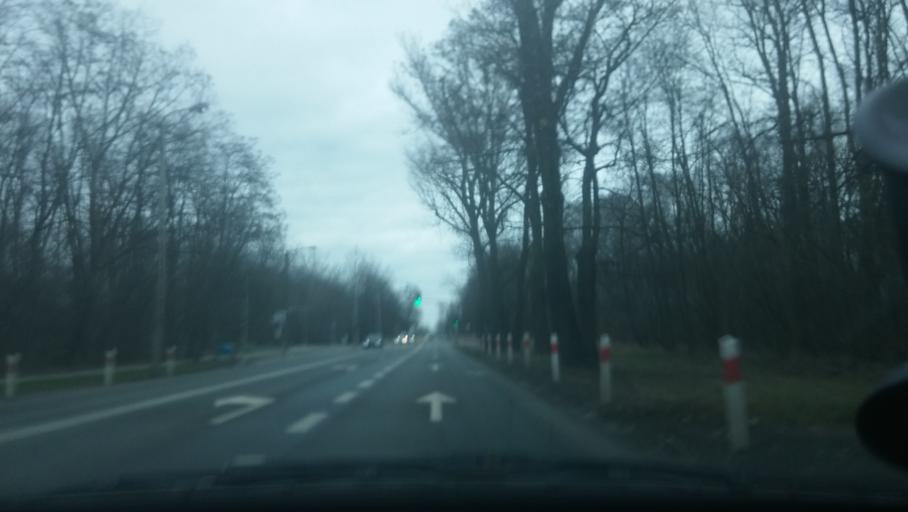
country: PL
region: Masovian Voivodeship
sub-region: Warszawa
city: Bialoleka
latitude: 52.3044
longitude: 21.0086
